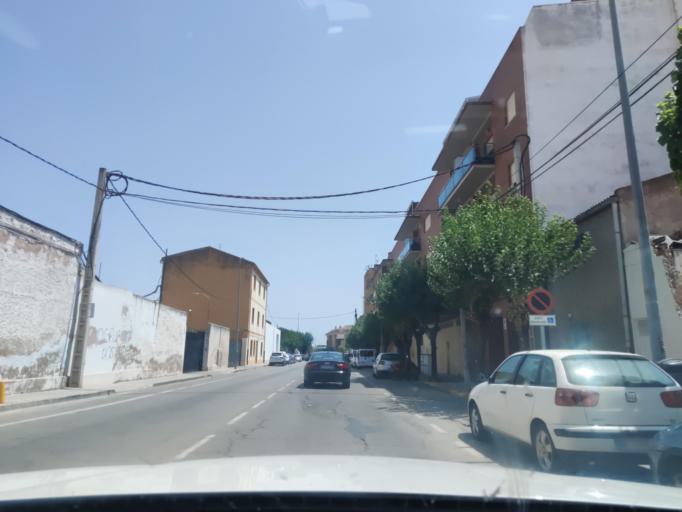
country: ES
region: Castille-La Mancha
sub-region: Provincia de Albacete
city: Hellin
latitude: 38.5085
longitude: -1.6903
